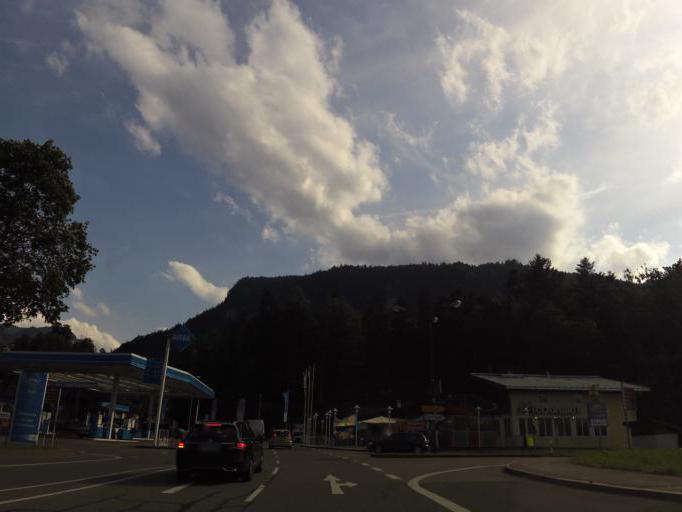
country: DE
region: Bavaria
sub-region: Upper Bavaria
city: Schoenau am Koenigssee
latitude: 47.5933
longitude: 12.9874
